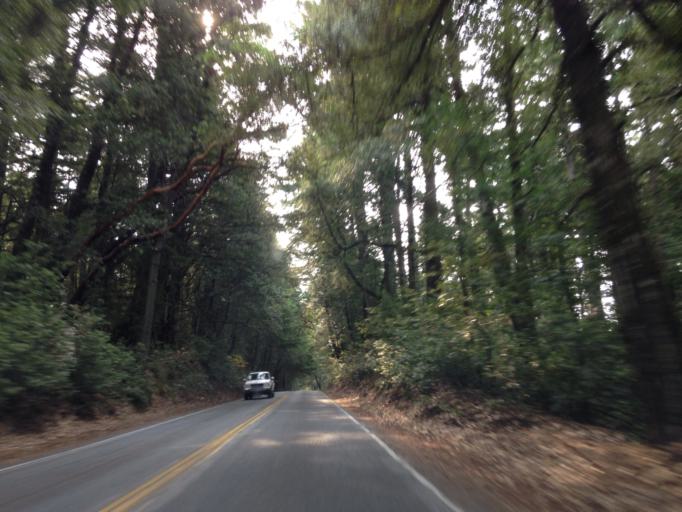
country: US
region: California
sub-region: San Mateo County
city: Woodside
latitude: 37.4165
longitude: -122.3161
